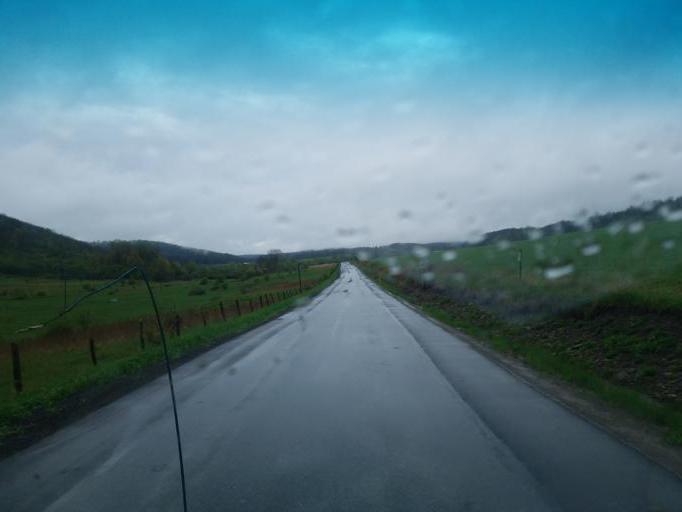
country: US
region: Pennsylvania
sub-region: Tioga County
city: Westfield
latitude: 41.9651
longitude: -77.6523
